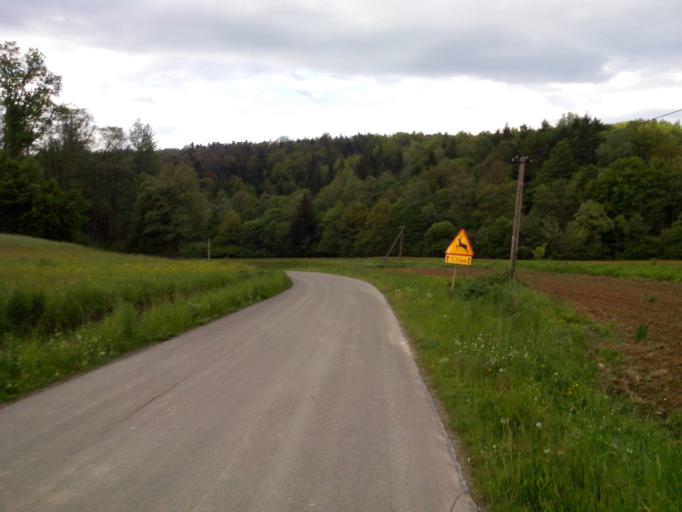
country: PL
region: Subcarpathian Voivodeship
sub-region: Powiat strzyzowski
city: Strzyzow
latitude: 49.8012
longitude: 21.8274
